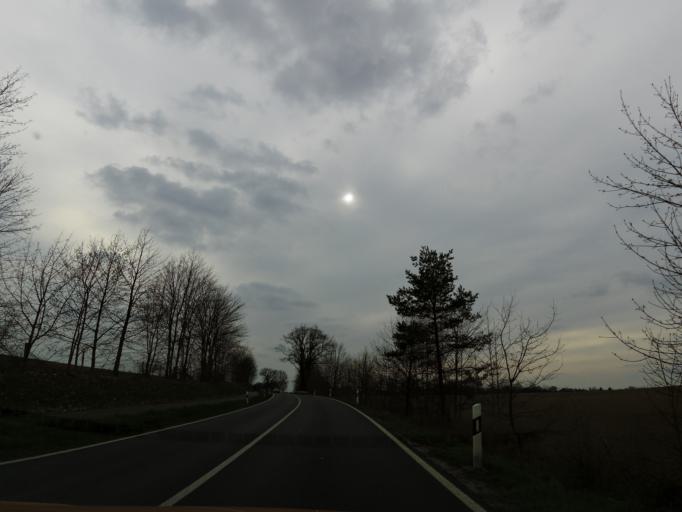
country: DE
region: Brandenburg
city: Mullrose
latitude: 52.2839
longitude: 14.4523
